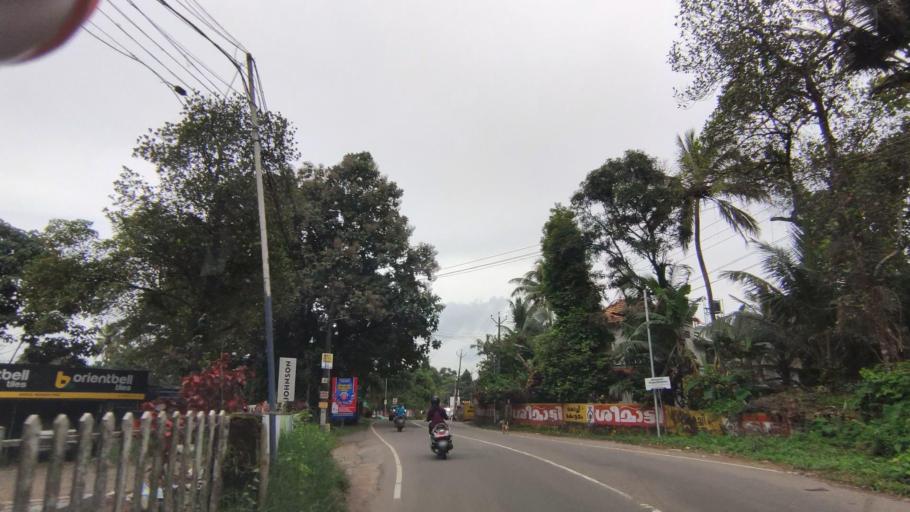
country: IN
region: Kerala
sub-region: Kottayam
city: Kottayam
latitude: 9.6229
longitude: 76.5115
